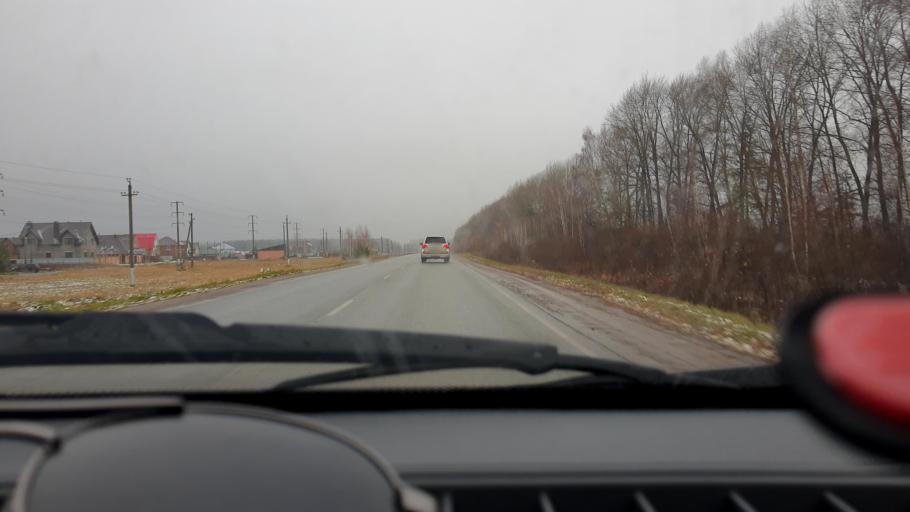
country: RU
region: Bashkortostan
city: Kabakovo
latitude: 54.6080
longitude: 56.1805
